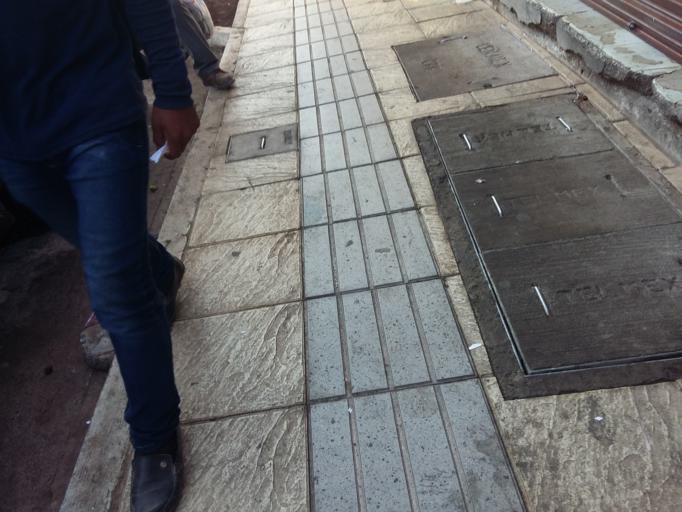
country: MX
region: Guerrero
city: Chilpancingo de los Bravos
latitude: 17.5509
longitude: -99.5008
